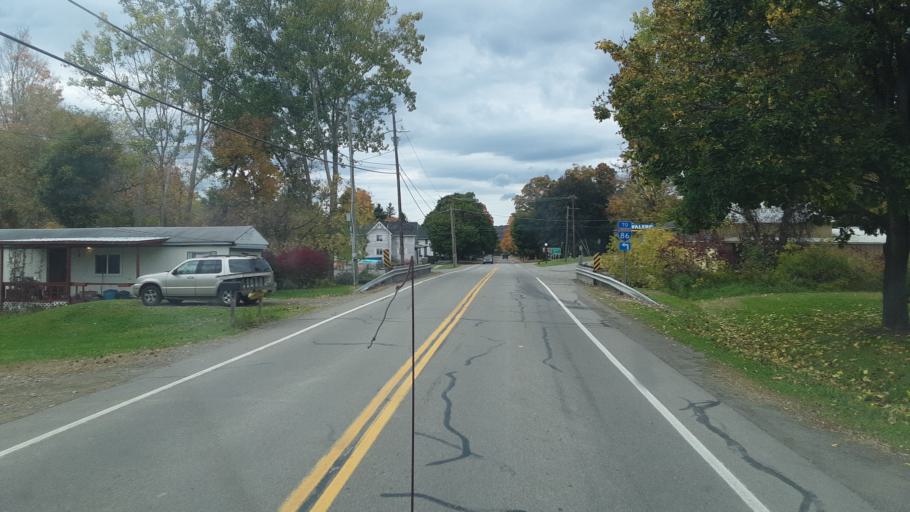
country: US
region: New York
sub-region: Allegany County
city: Belmont
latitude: 42.3038
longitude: -78.0076
